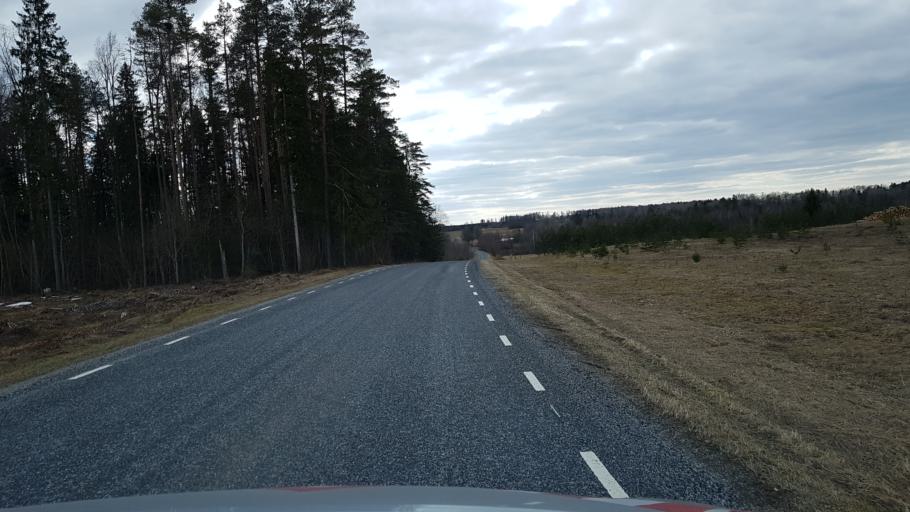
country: EE
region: Laeaene-Virumaa
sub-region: Tamsalu vald
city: Tamsalu
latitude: 59.2128
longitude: 26.1538
